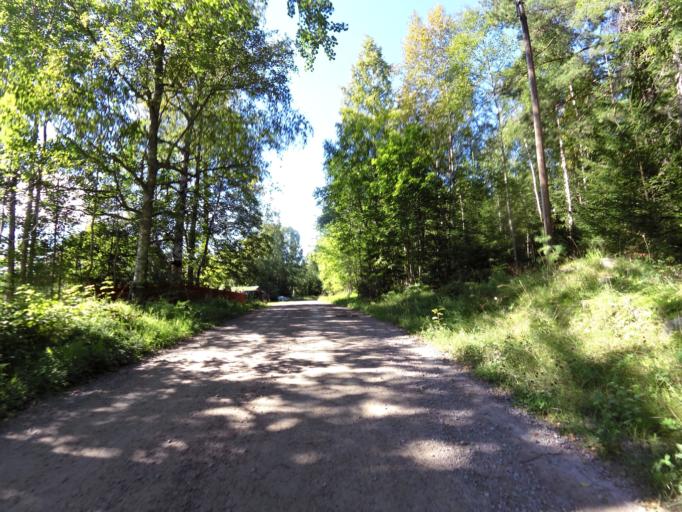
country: SE
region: Gaevleborg
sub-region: Hofors Kommun
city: Hofors
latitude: 60.5330
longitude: 16.4121
